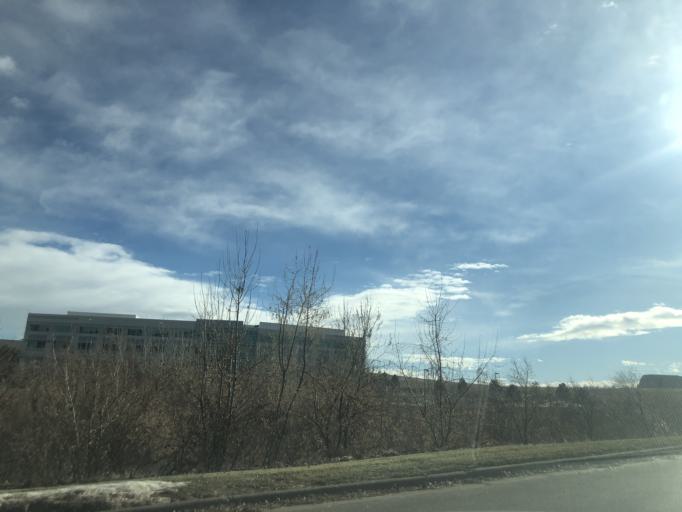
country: US
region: Colorado
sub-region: Douglas County
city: Meridian
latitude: 39.5594
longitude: -104.8625
